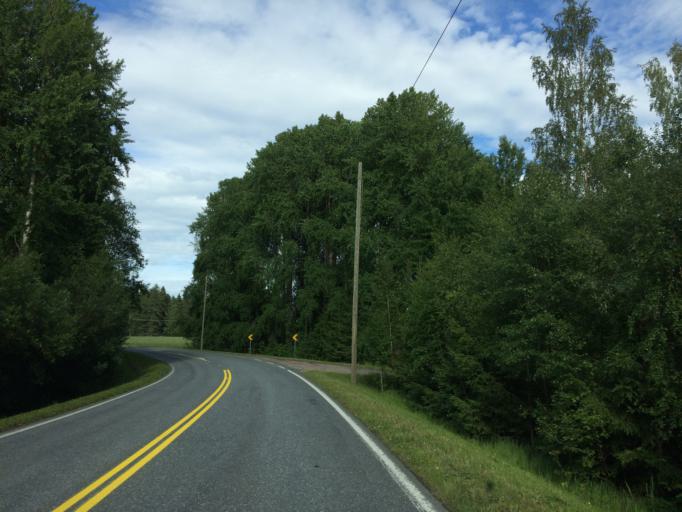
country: FI
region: Haeme
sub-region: Haemeenlinna
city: Janakkala
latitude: 60.8836
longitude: 24.5851
